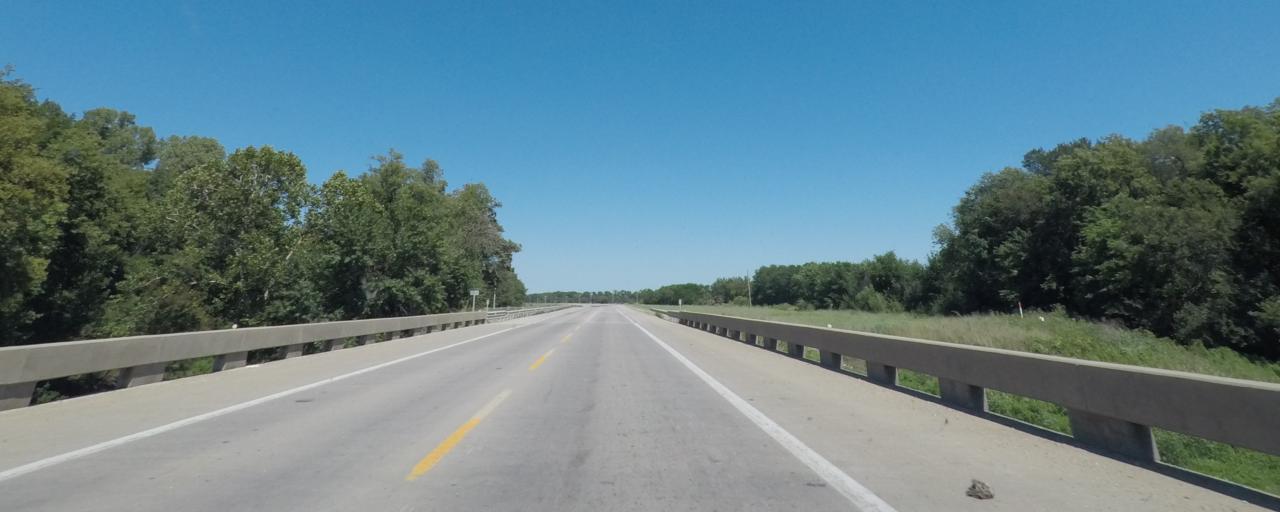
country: US
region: Kansas
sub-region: Chase County
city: Cottonwood Falls
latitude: 38.3783
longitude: -96.6450
